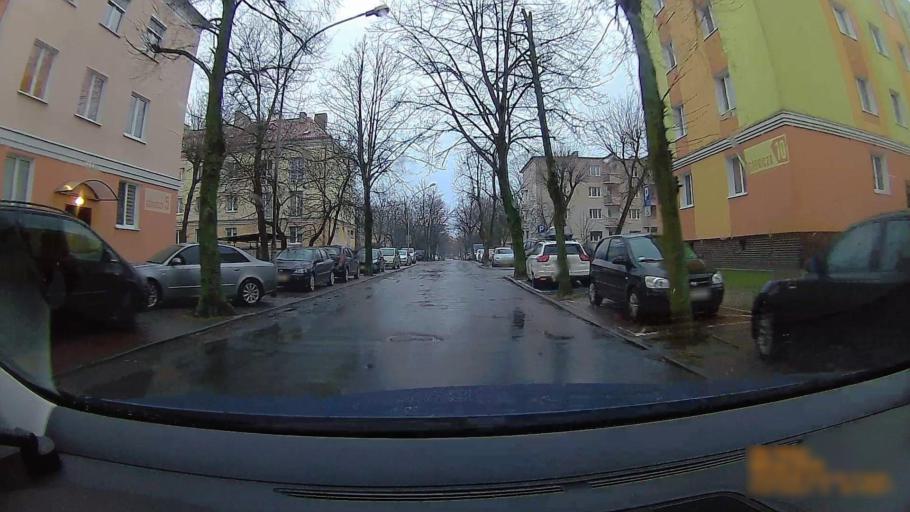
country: PL
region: Greater Poland Voivodeship
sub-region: Konin
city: Konin
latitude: 52.2291
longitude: 18.2557
